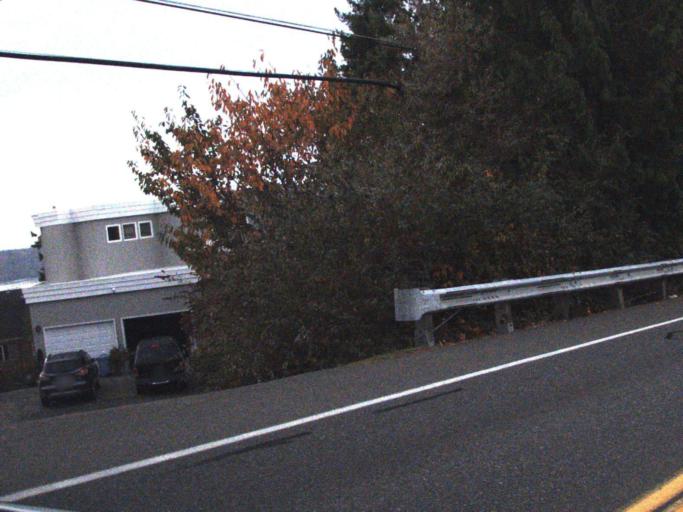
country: US
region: Washington
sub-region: Snohomish County
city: Mukilteo
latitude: 47.9310
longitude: -122.3050
